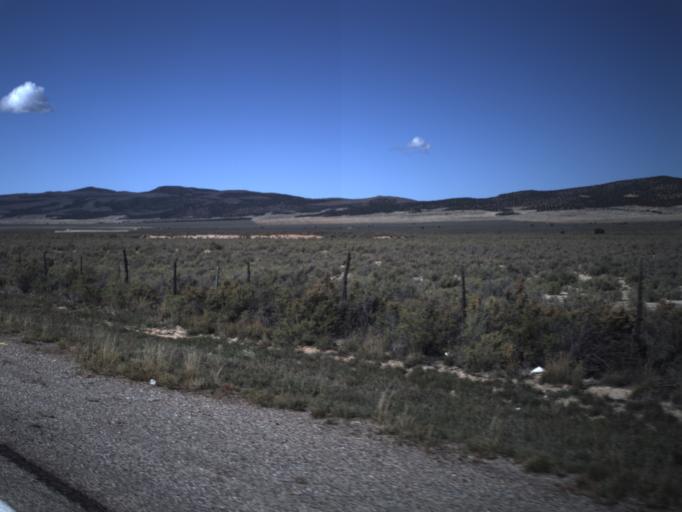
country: US
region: Utah
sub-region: Iron County
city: Cedar City
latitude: 37.6696
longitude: -113.1937
